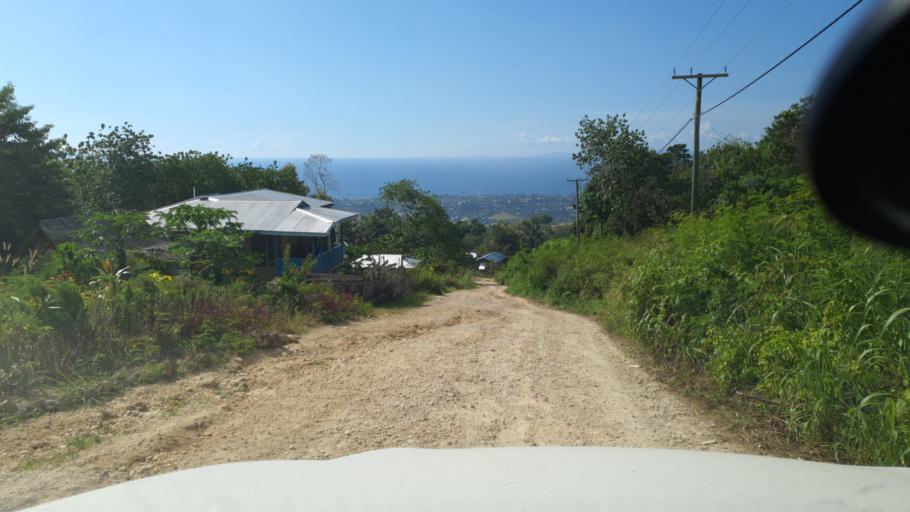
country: SB
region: Guadalcanal
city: Honiara
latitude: -9.4653
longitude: 159.9749
